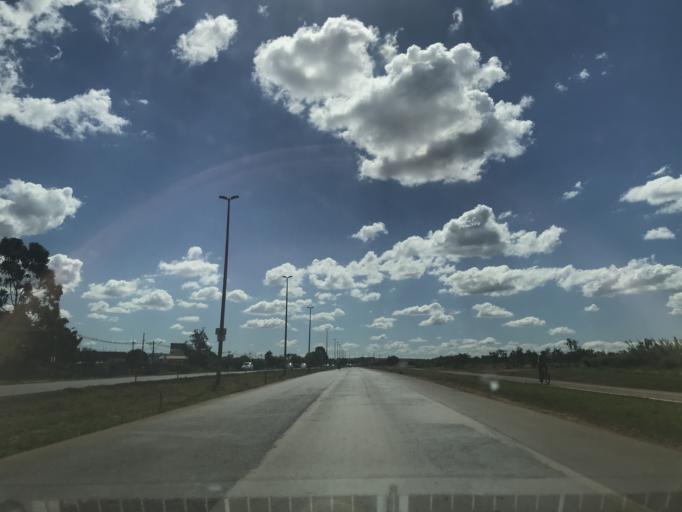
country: BR
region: Federal District
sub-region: Brasilia
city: Brasilia
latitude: -15.8066
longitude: -48.0008
